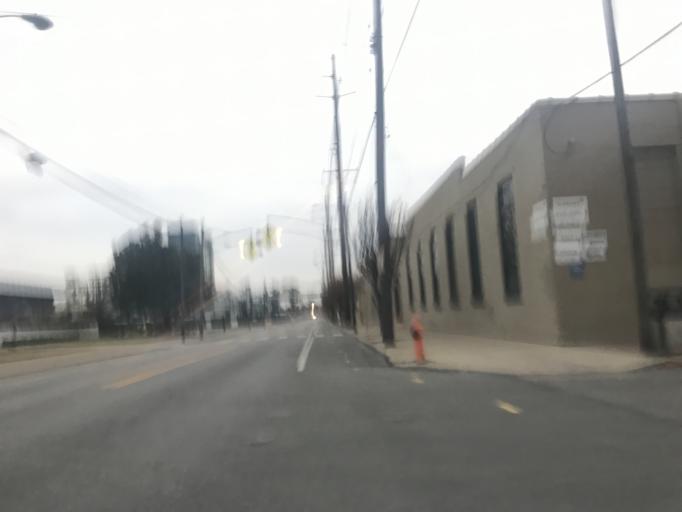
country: US
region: Kentucky
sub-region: Jefferson County
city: Louisville
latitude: 38.2352
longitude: -85.7739
